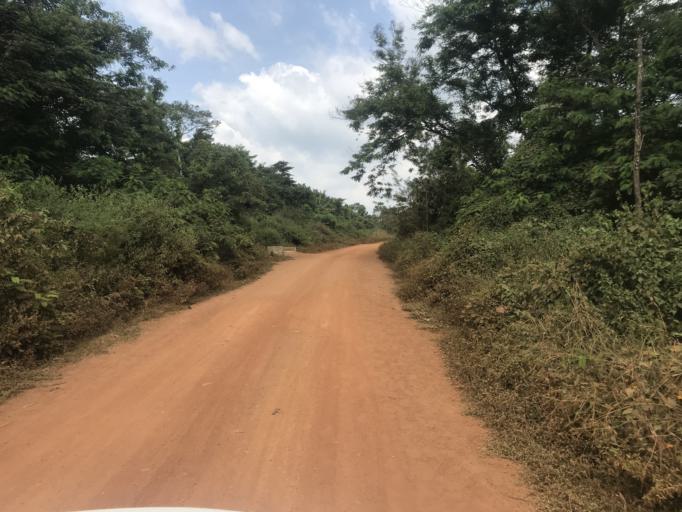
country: NG
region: Osun
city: Inisa
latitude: 7.8593
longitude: 4.3820
